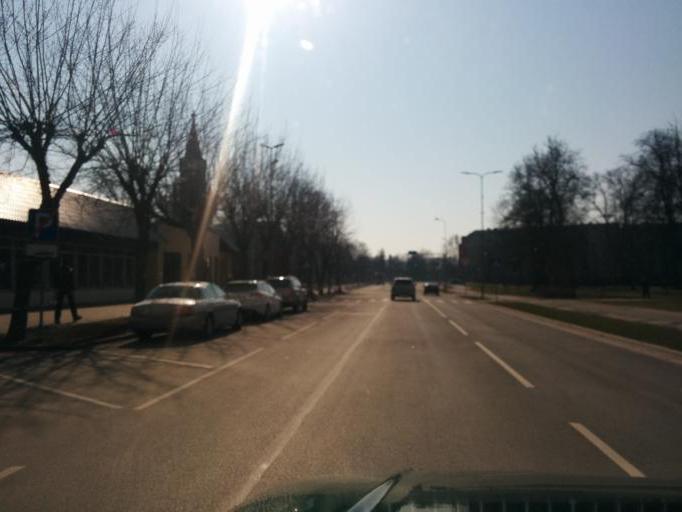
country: LV
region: Jelgava
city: Jelgava
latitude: 56.6454
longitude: 23.7270
